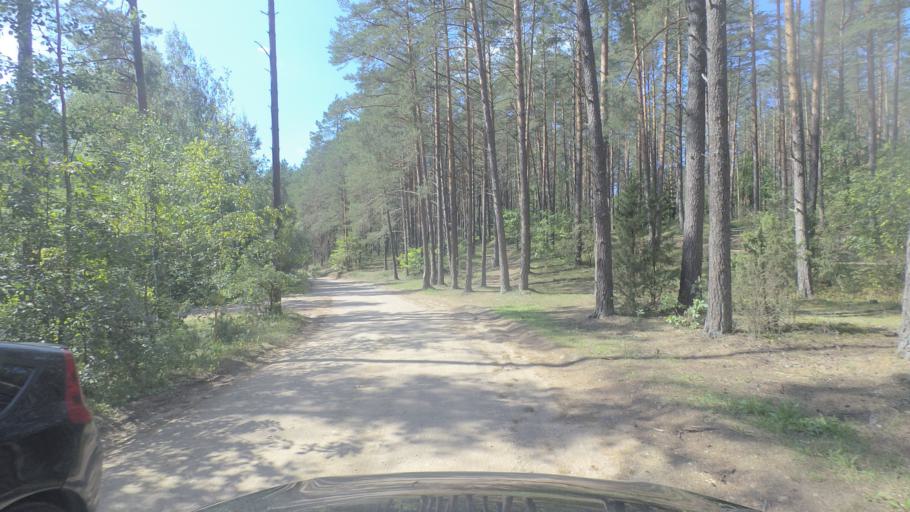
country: LT
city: Nemencine
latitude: 54.8487
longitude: 25.5012
